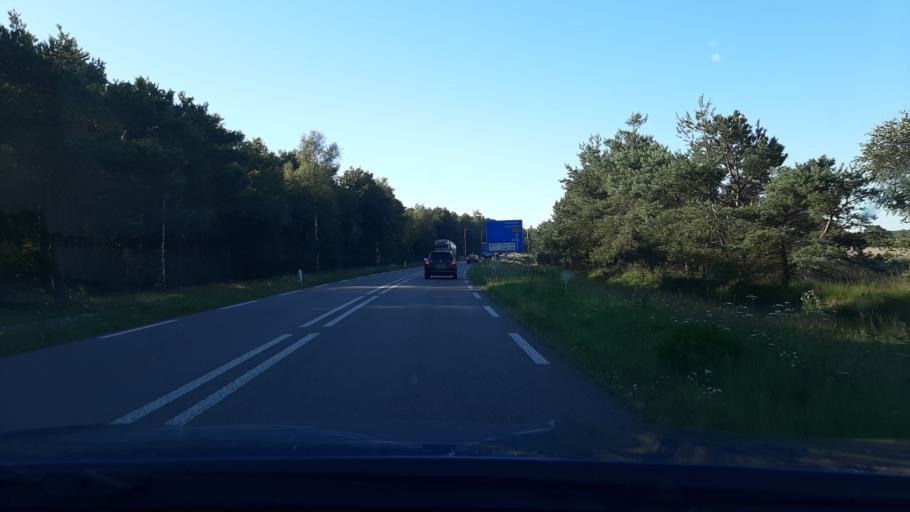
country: NL
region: Gelderland
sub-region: Gemeente Apeldoorn
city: Uddel
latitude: 52.2594
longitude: 5.7434
